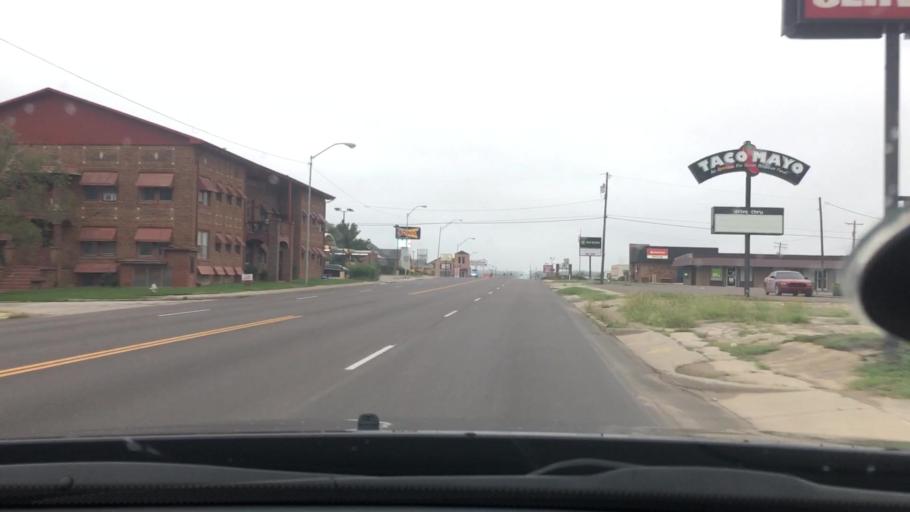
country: US
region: Oklahoma
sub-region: Seminole County
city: Seminole
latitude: 35.2276
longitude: -96.6710
